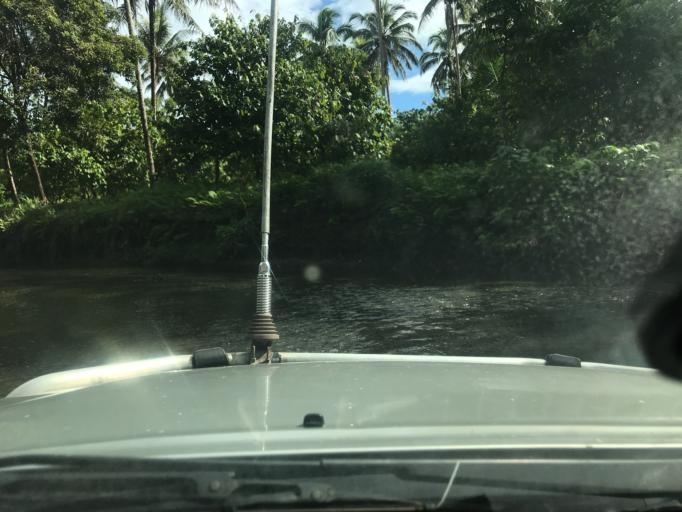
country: SB
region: Malaita
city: Auki
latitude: -8.9332
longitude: 160.7677
